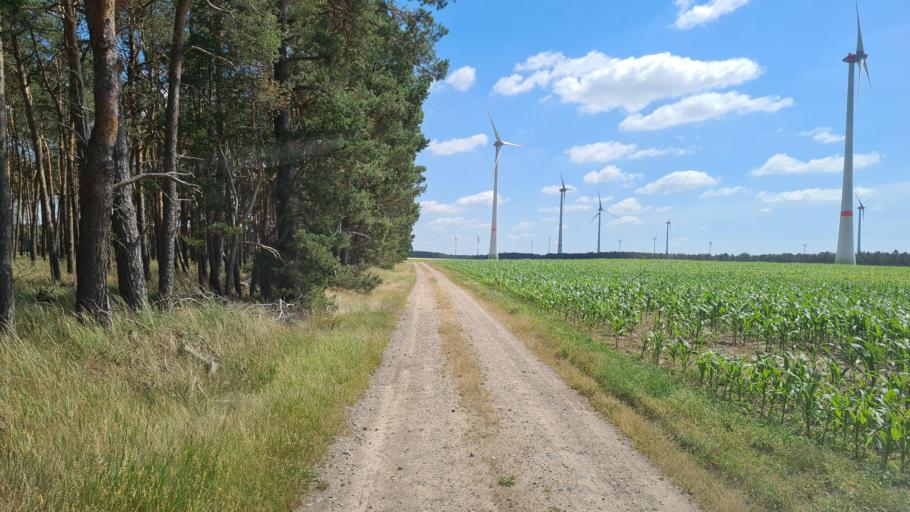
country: DE
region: Brandenburg
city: Treuenbrietzen
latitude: 52.0316
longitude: 12.8496
